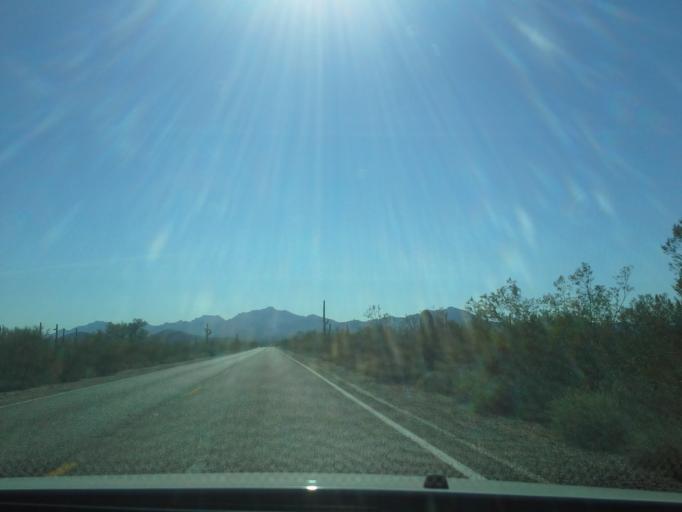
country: MX
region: Sonora
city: Sonoyta
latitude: 31.8972
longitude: -112.8118
